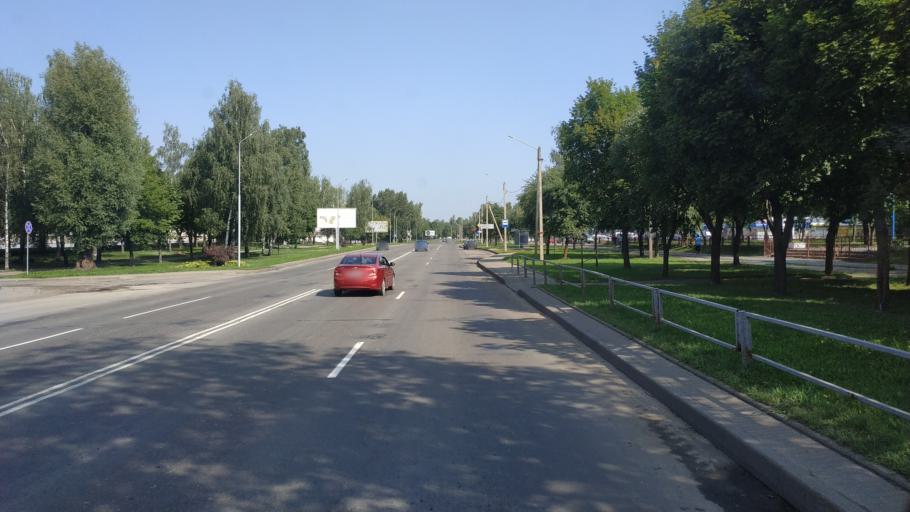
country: BY
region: Mogilev
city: Buynichy
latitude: 53.8714
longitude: 30.3132
